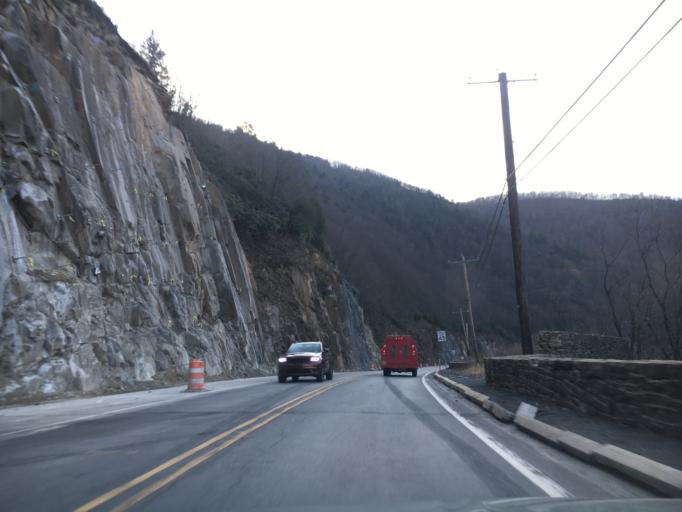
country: US
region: Pennsylvania
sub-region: Carbon County
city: Jim Thorpe
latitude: 40.8593
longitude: -75.7309
